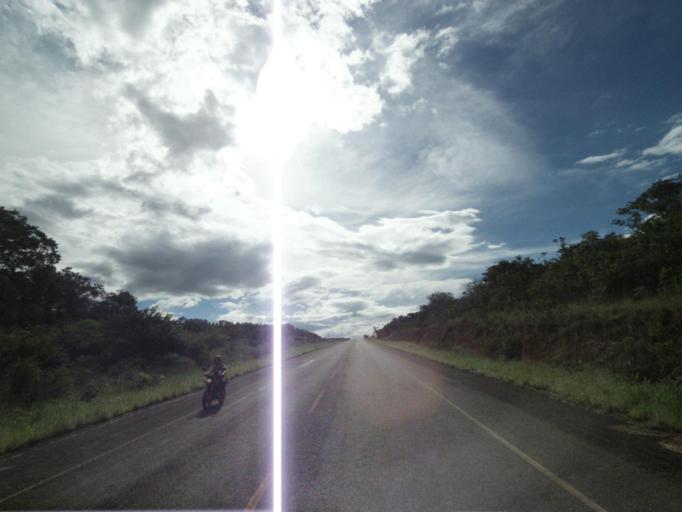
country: BR
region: Goias
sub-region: Jaragua
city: Jaragua
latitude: -15.8388
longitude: -49.3009
